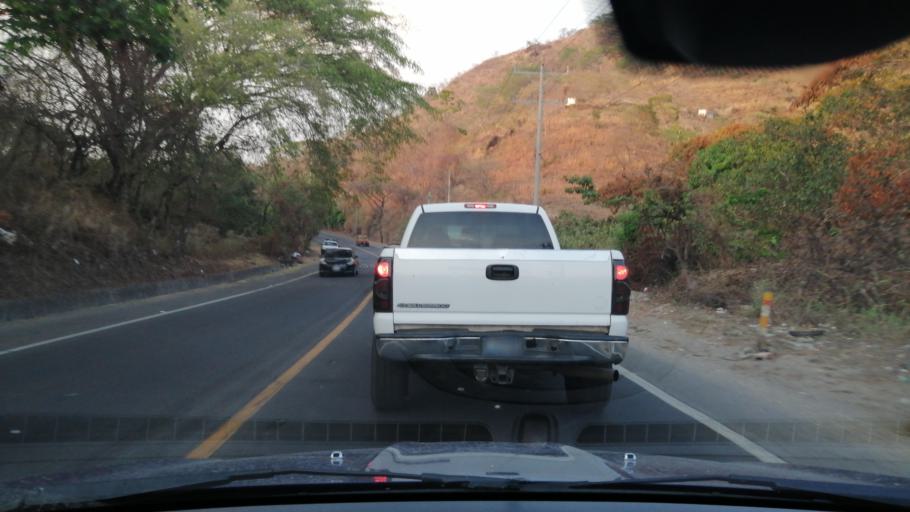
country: SV
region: Santa Ana
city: Santa Ana
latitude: 13.9903
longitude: -89.5423
